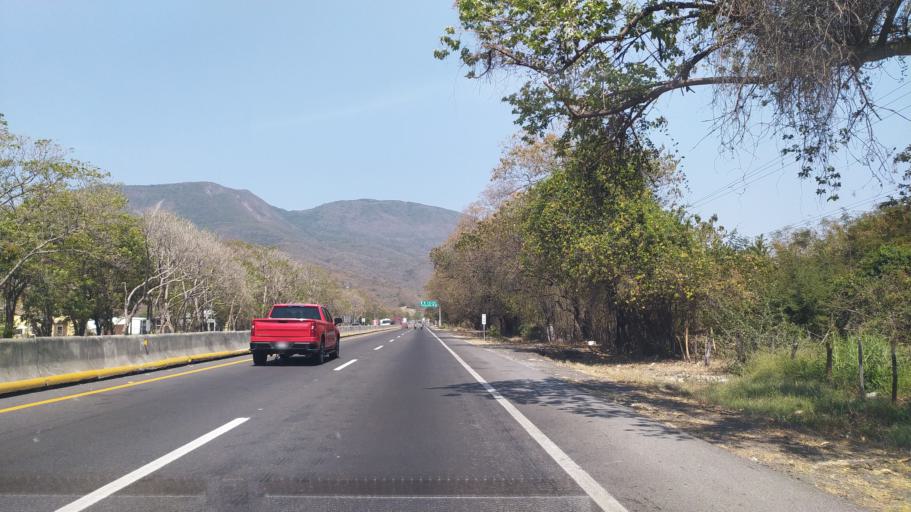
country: MX
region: Colima
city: Madrid
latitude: 19.0103
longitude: -103.8323
